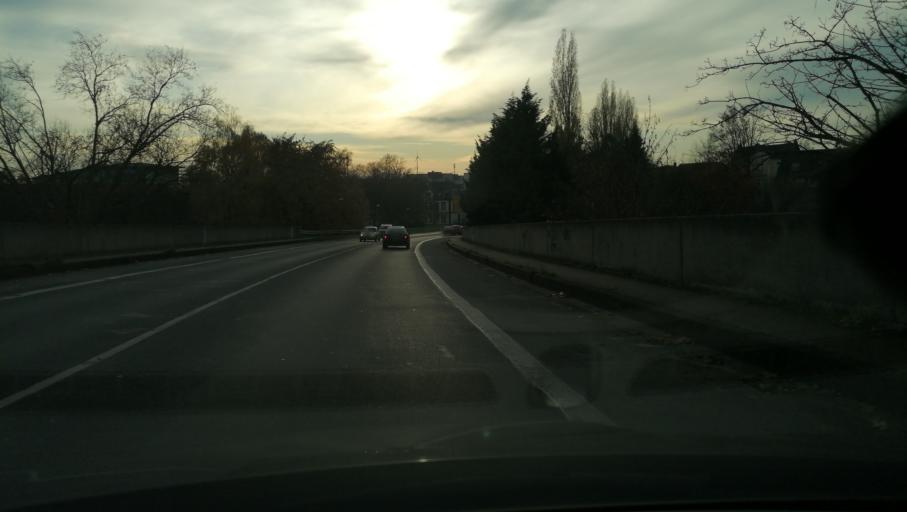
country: DE
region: North Rhine-Westphalia
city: Waltrop
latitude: 51.5693
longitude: 7.3760
